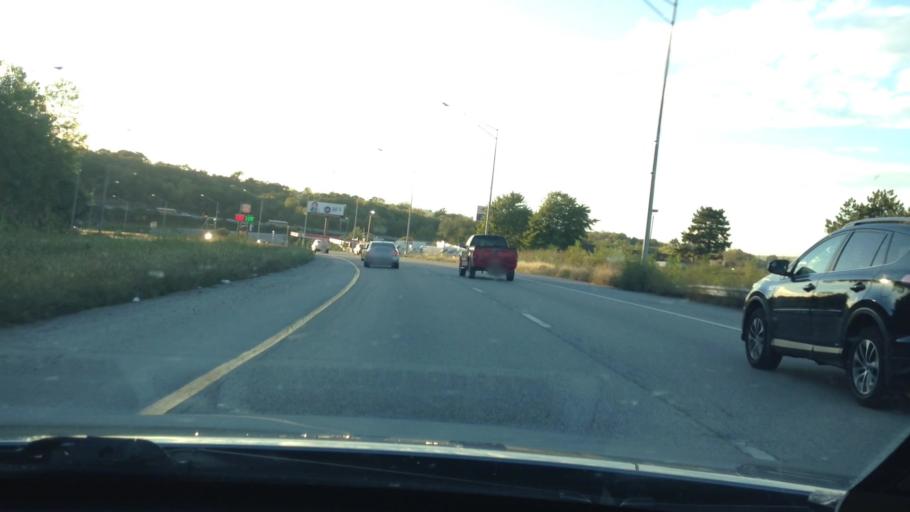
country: US
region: Missouri
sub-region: Clay County
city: Claycomo
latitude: 39.1599
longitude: -94.4901
